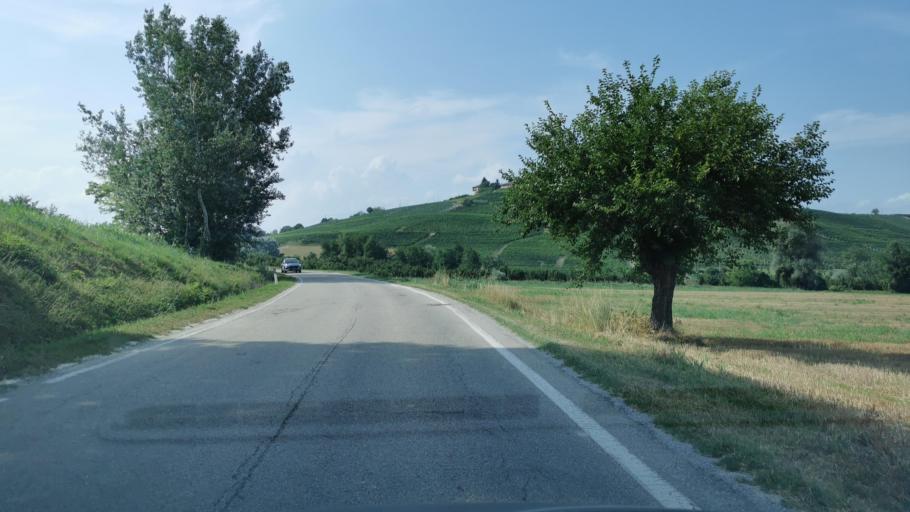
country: IT
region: Piedmont
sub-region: Provincia di Cuneo
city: Roddi
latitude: 44.6569
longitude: 7.9661
